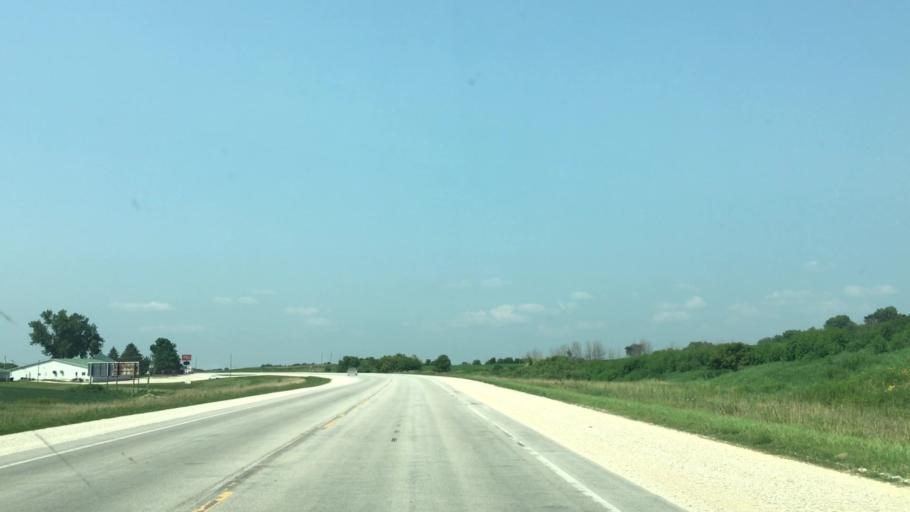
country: US
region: Iowa
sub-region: Winneshiek County
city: Decorah
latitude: 43.3616
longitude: -91.8042
